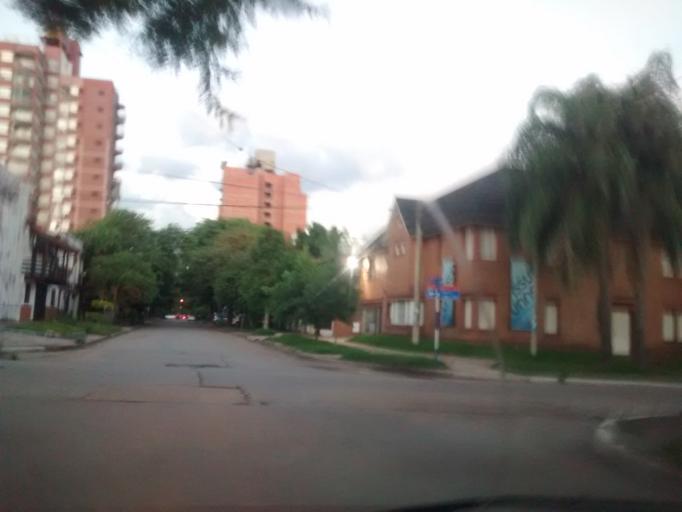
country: AR
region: Chaco
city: Resistencia
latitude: -27.4488
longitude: -58.9788
